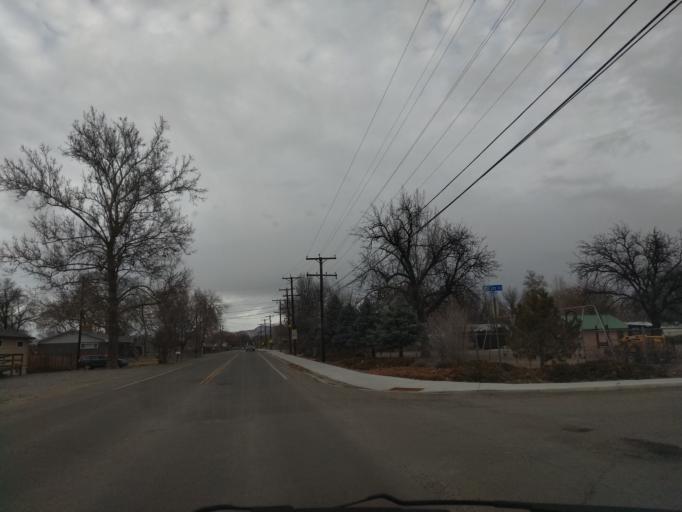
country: US
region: Colorado
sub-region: Mesa County
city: Fruitvale
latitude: 39.0808
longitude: -108.5198
